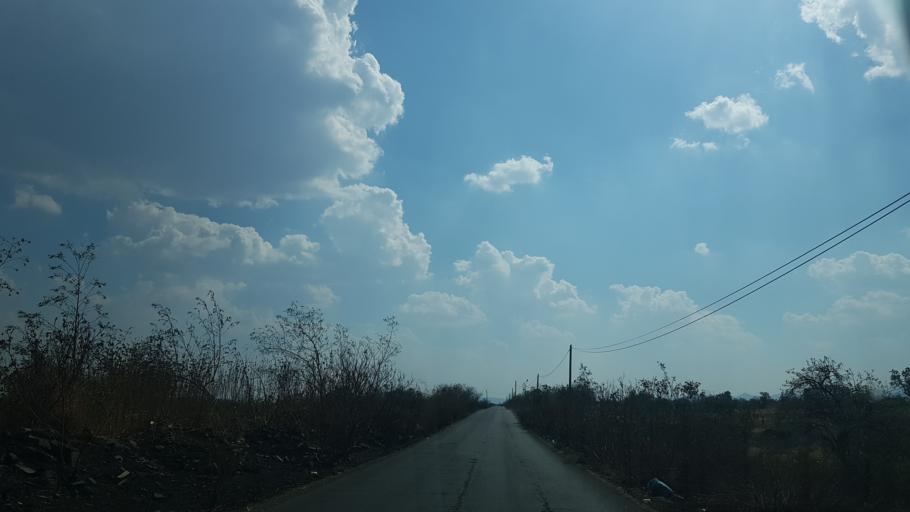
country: MX
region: Puebla
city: Atlixco
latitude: 18.9071
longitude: -98.4792
